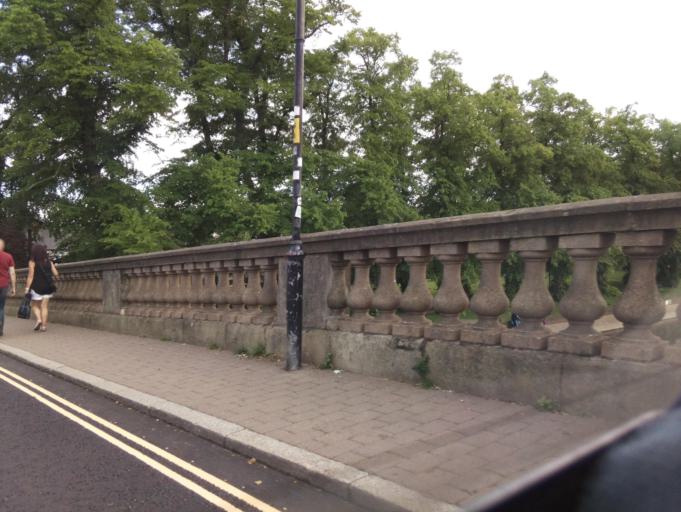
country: GB
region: England
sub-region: Worcestershire
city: Evesham
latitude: 52.0915
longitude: -1.9428
